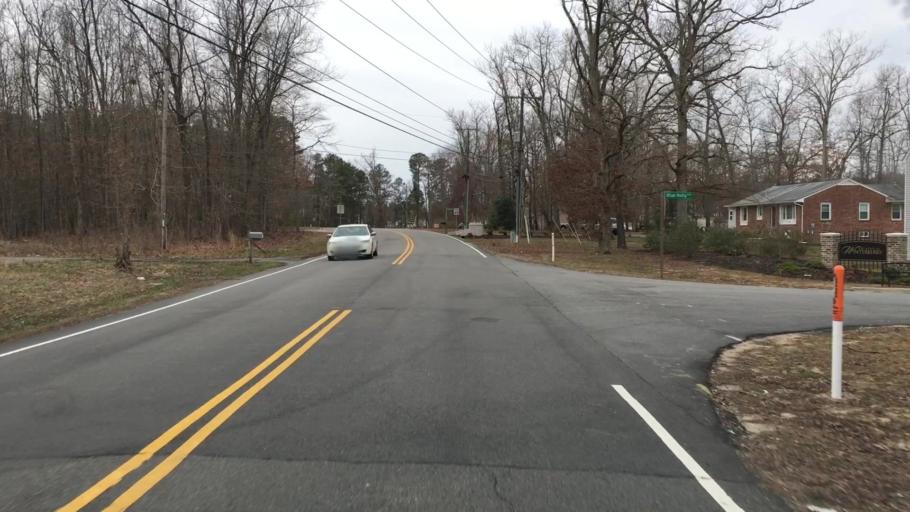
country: US
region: Virginia
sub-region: Henrico County
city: Glen Allen
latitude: 37.6710
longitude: -77.5566
